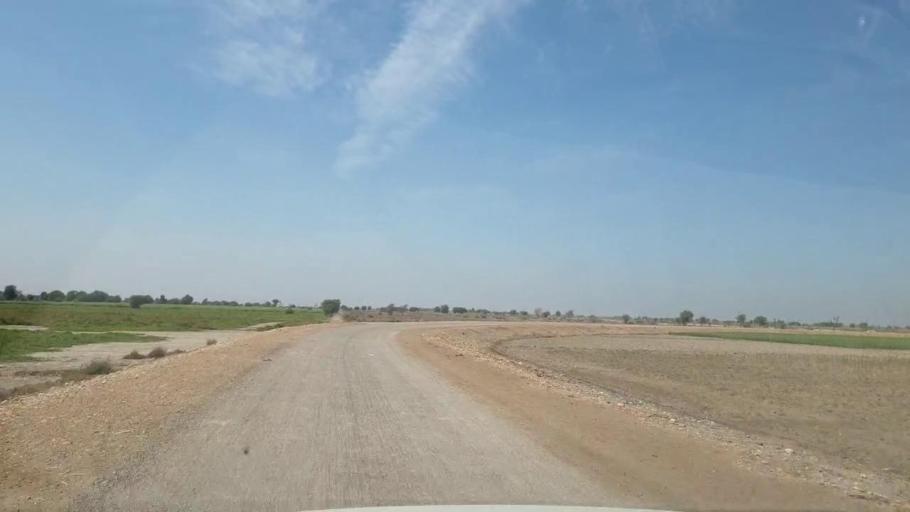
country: PK
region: Sindh
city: Mirpur Khas
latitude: 25.6311
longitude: 69.1983
